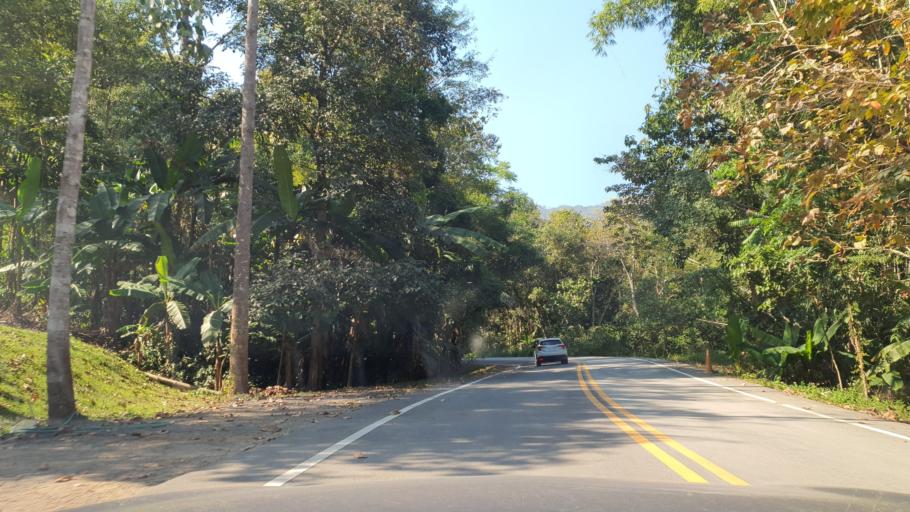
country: TH
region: Chiang Rai
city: Mae Lao
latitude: 19.8742
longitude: 99.6277
